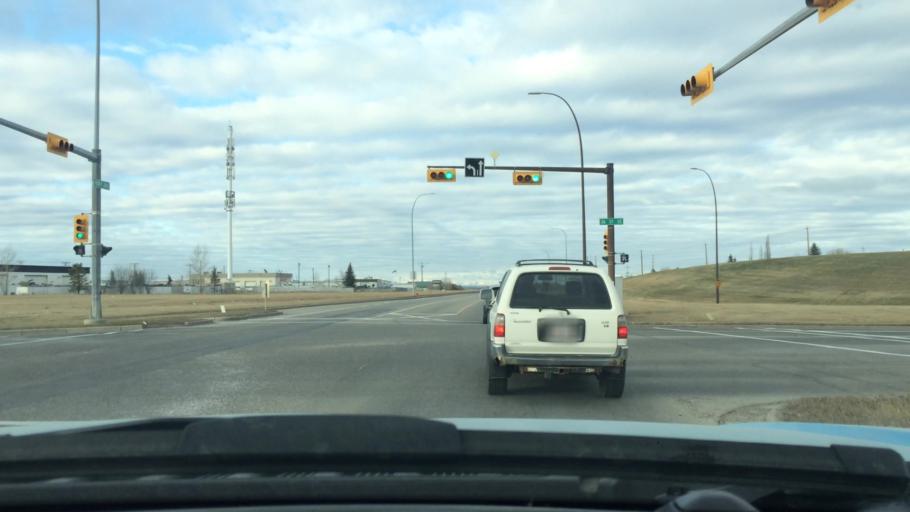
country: CA
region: Alberta
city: Calgary
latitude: 51.0150
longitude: -113.9766
